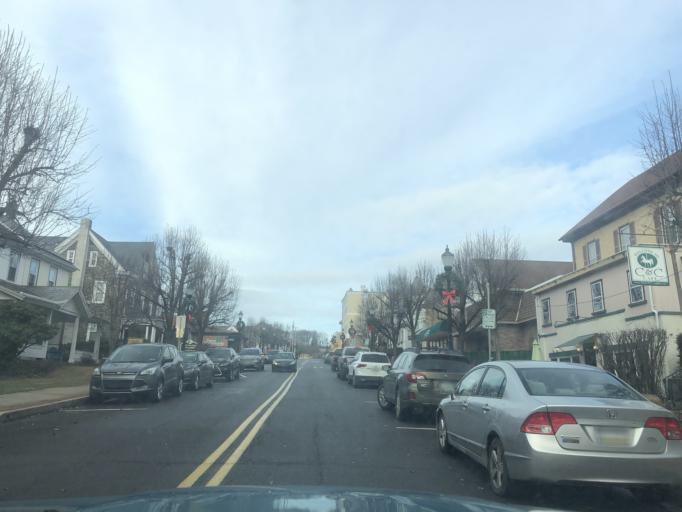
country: US
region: Pennsylvania
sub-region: Bucks County
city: Perkasie
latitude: 40.3739
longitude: -75.2945
